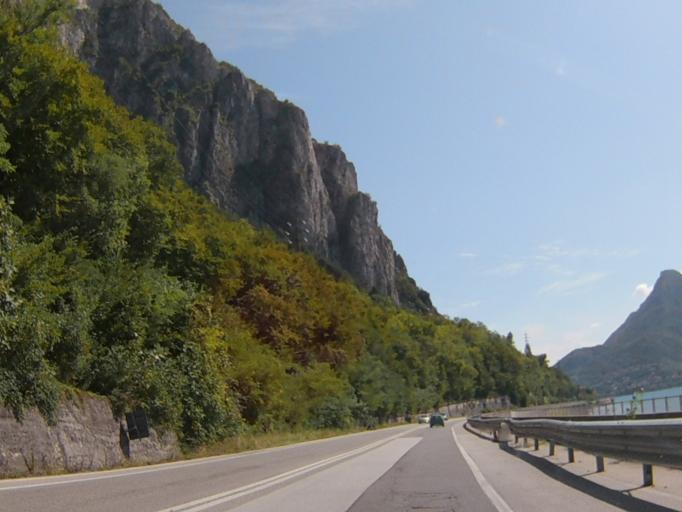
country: IT
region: Lombardy
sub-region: Provincia di Lecco
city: Lecco
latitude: 45.8752
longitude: 9.3768
